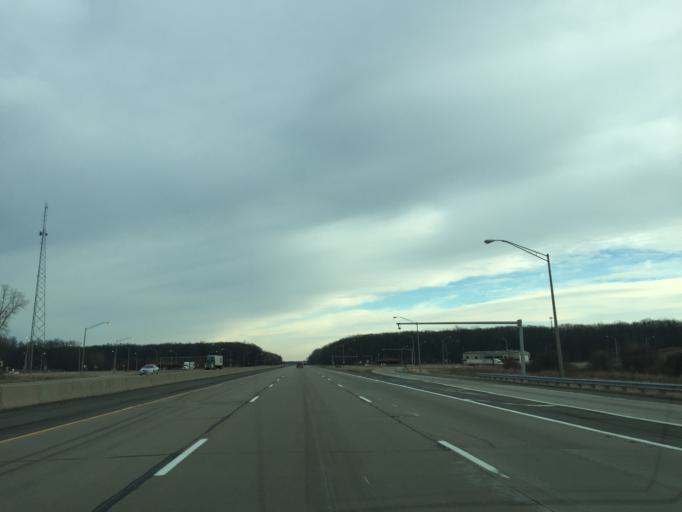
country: US
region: Indiana
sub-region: Porter County
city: Chesterton
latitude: 41.6392
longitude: -87.0005
